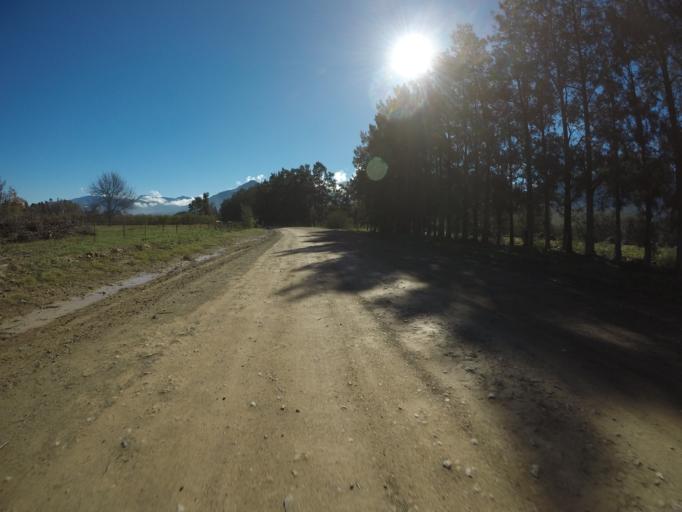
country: ZA
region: Western Cape
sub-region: Overberg District Municipality
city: Caledon
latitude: -34.0770
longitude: 19.6438
